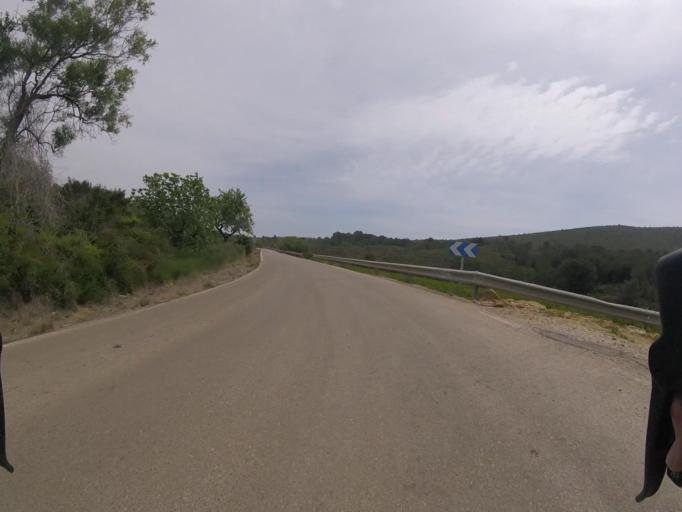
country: ES
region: Valencia
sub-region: Provincia de Castello
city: Cabanes
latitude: 40.1545
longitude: 0.0564
